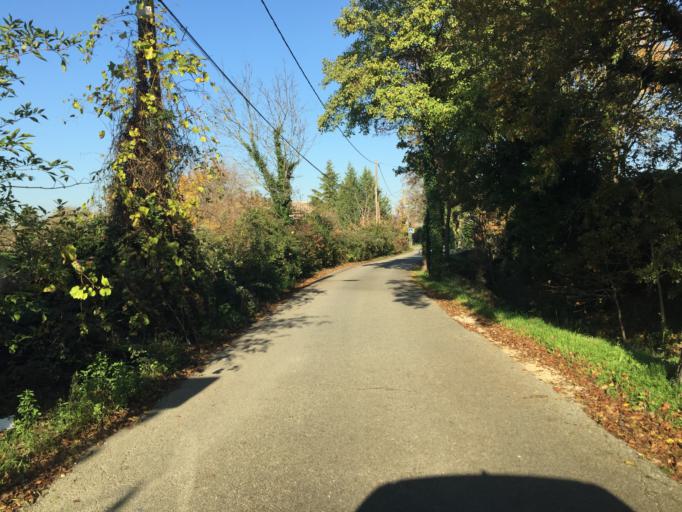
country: FR
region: Provence-Alpes-Cote d'Azur
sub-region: Departement du Vaucluse
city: Entraigues-sur-la-Sorgue
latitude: 44.0060
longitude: 4.9232
